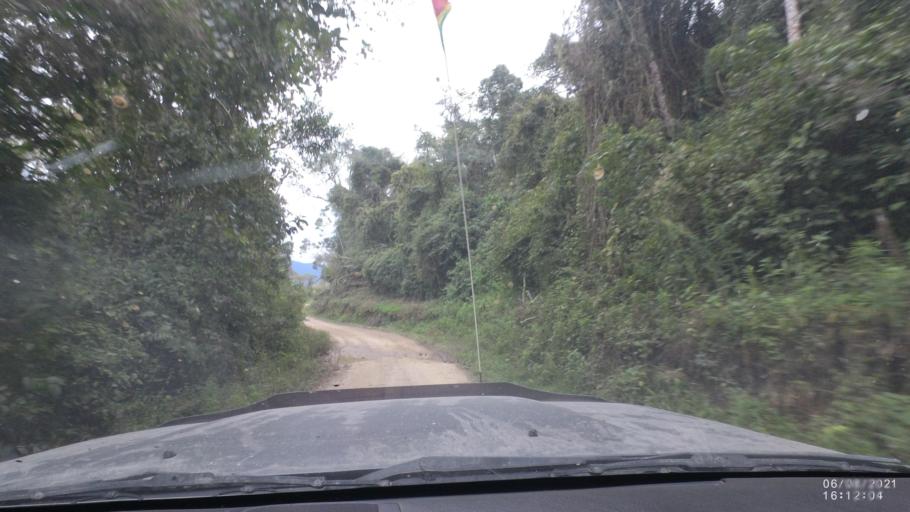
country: BO
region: La Paz
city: Quime
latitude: -16.5579
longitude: -66.7370
